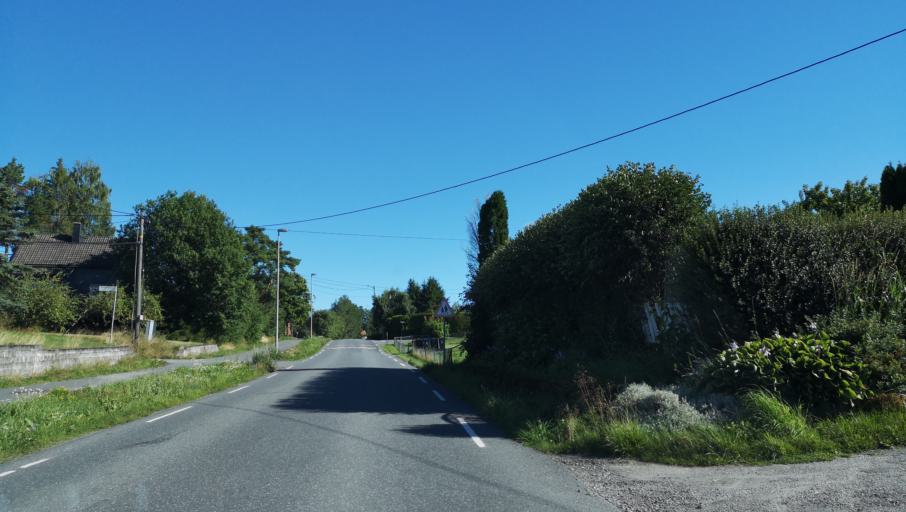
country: NO
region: Ostfold
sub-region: Hobol
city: Knappstad
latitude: 59.6236
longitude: 11.0245
